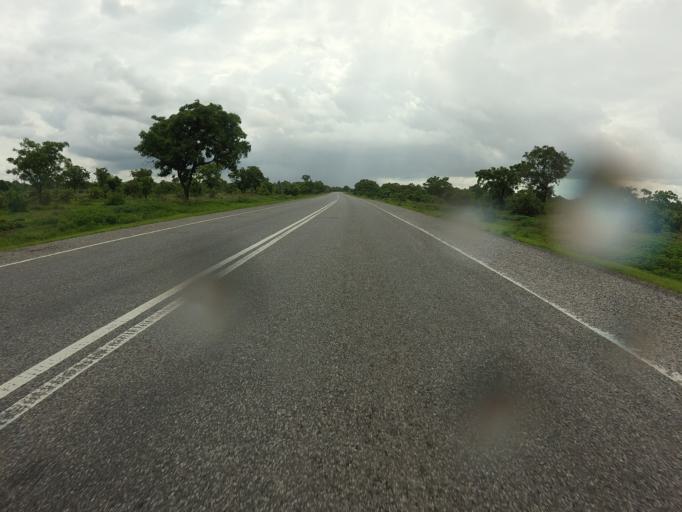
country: GH
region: Northern
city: Tamale
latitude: 9.1359
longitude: -1.3401
